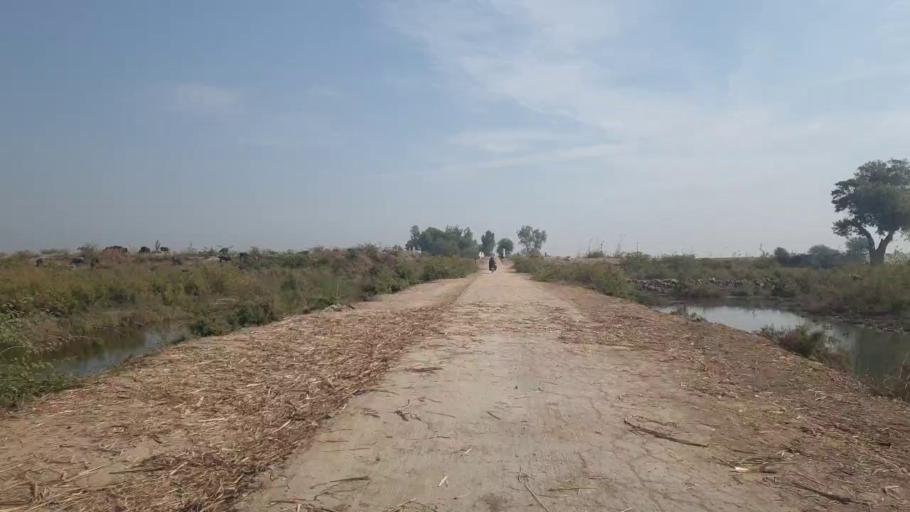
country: PK
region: Sindh
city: Mirwah Gorchani
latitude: 25.3763
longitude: 69.1901
